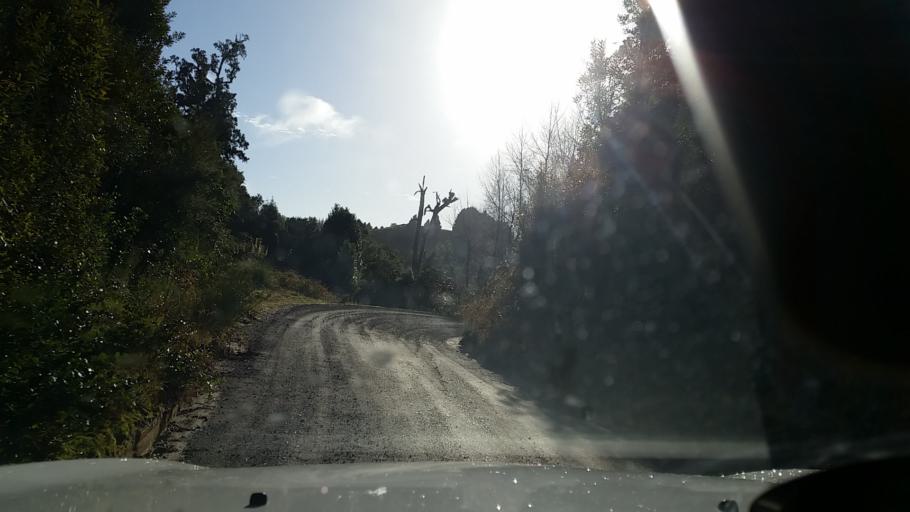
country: NZ
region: Bay of Plenty
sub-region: Kawerau District
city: Kawerau
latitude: -38.0032
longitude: 176.5973
